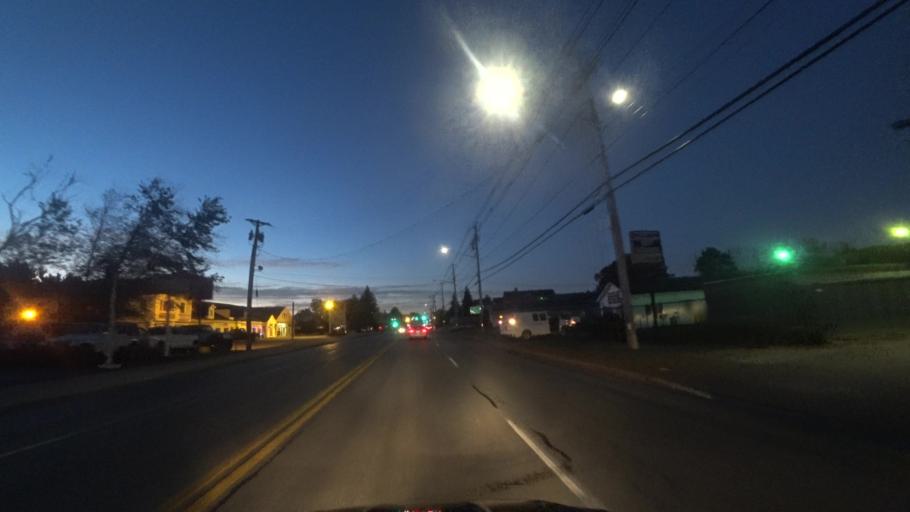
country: US
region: Massachusetts
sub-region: Middlesex County
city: North Reading
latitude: 42.5798
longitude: -71.1120
